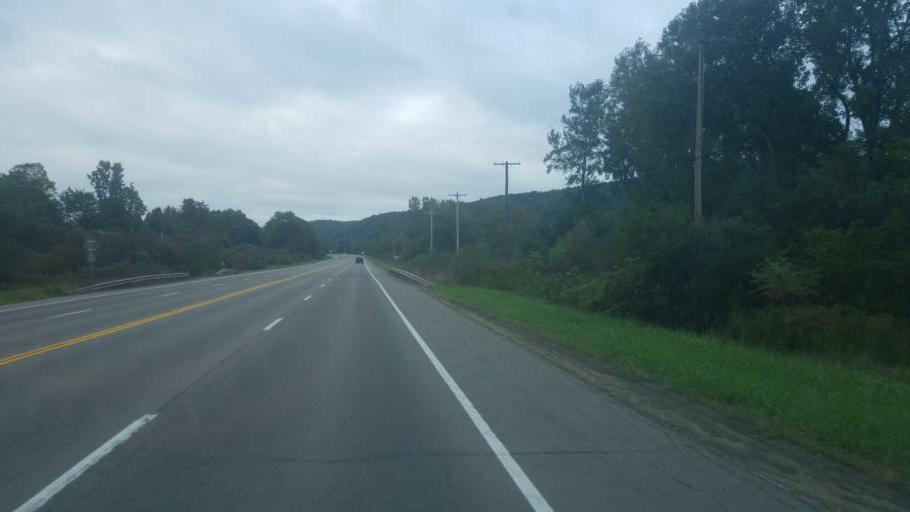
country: US
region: New York
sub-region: Cattaraugus County
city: Weston Mills
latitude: 42.1675
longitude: -78.3910
